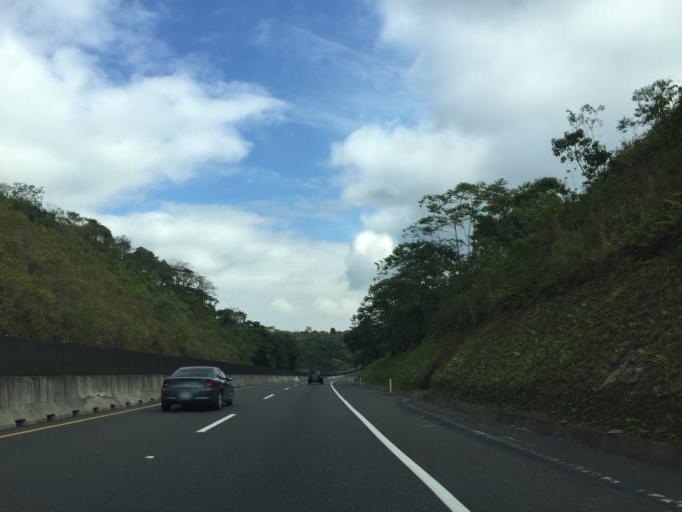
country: MX
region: Puebla
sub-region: Xicotepec
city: San Lorenzo
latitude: 20.3997
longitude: -97.9442
